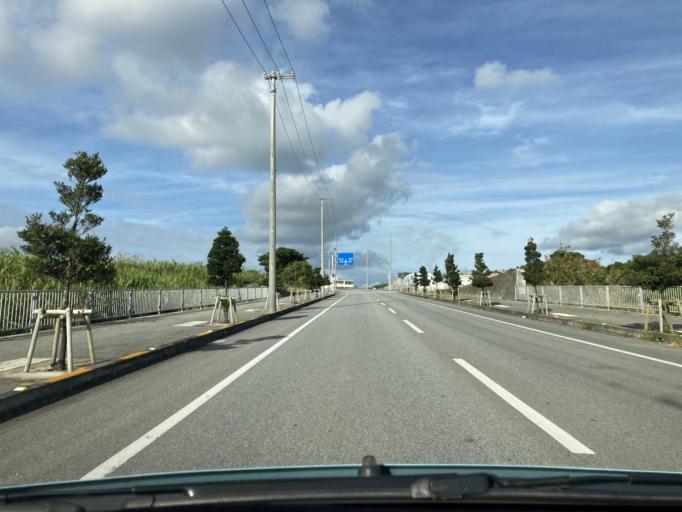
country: JP
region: Okinawa
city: Itoman
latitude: 26.1280
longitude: 127.6829
